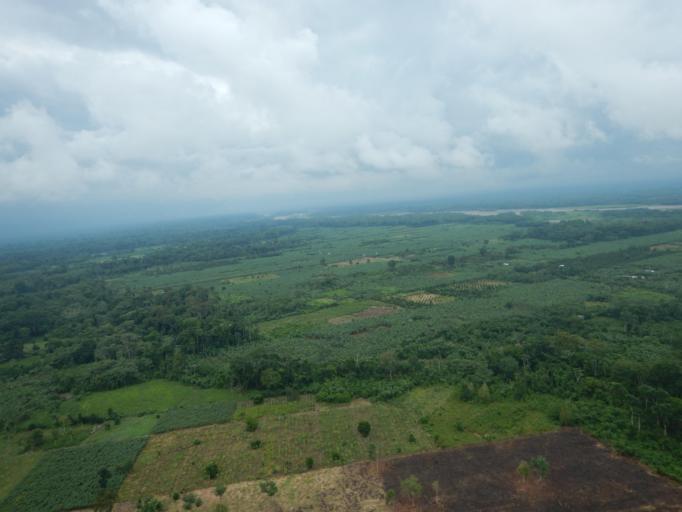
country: BO
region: Cochabamba
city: Chimore
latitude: -17.1455
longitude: -64.8030
